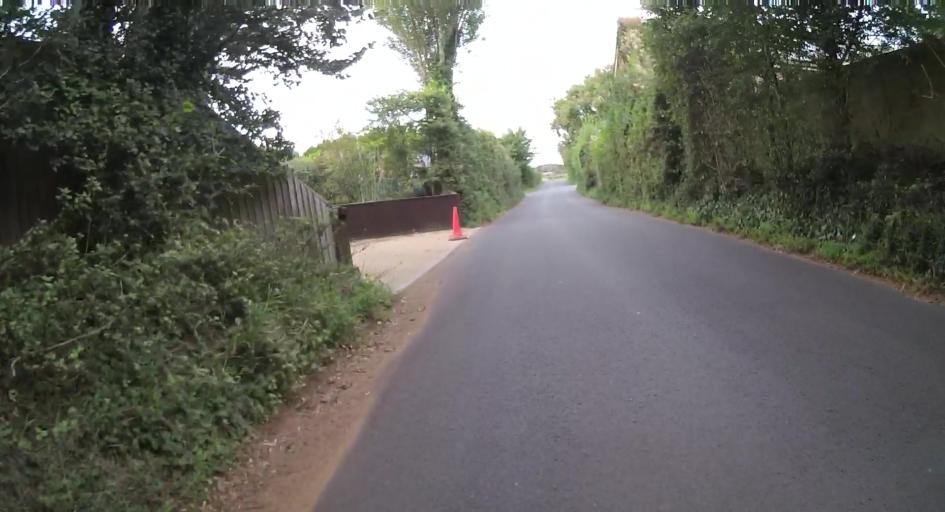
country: GB
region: England
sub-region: Isle of Wight
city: Freshwater
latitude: 50.6777
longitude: -1.4962
